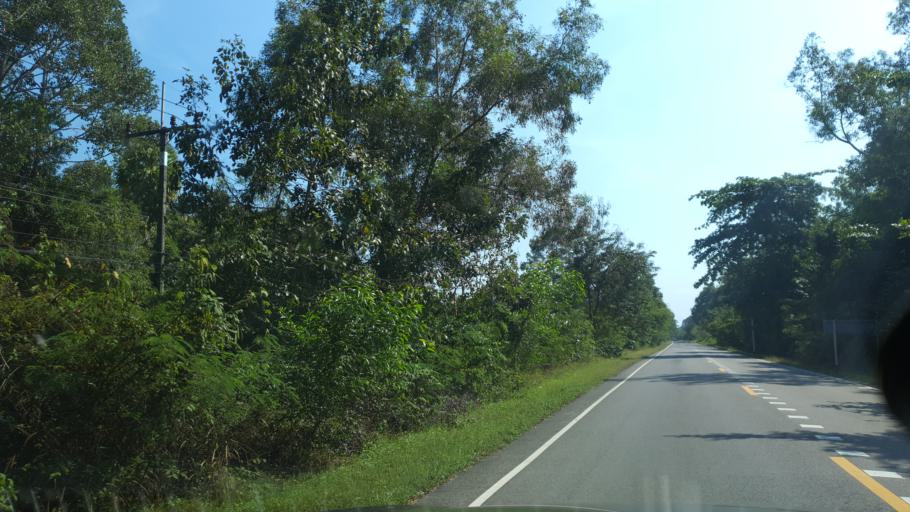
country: TH
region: Surat Thani
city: Tha Chana
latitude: 9.5845
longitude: 99.2024
